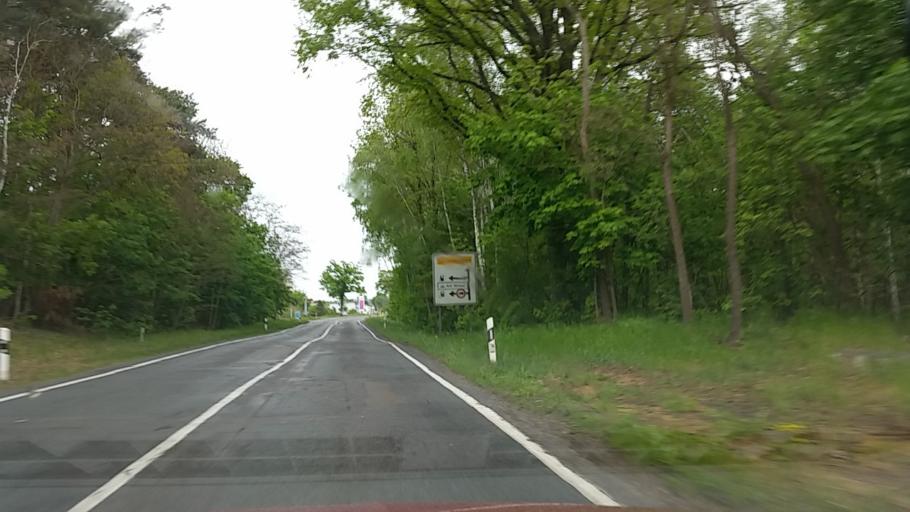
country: DE
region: Brandenburg
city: Spreenhagen
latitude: 52.3231
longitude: 13.9013
